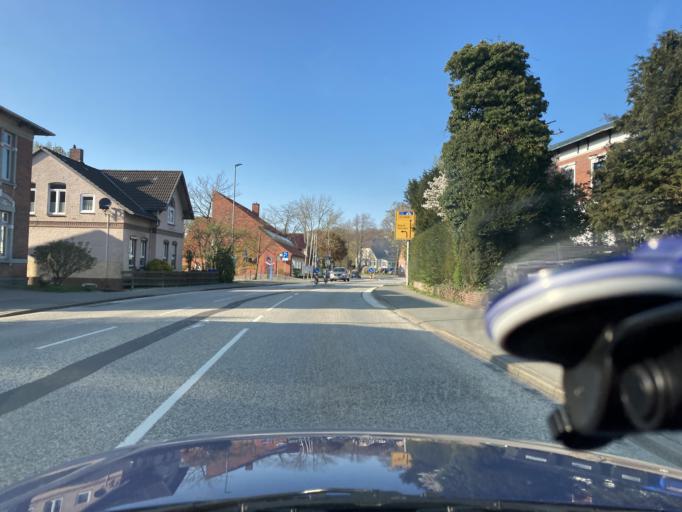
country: DE
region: Schleswig-Holstein
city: Meldorf
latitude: 54.0908
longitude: 9.0689
